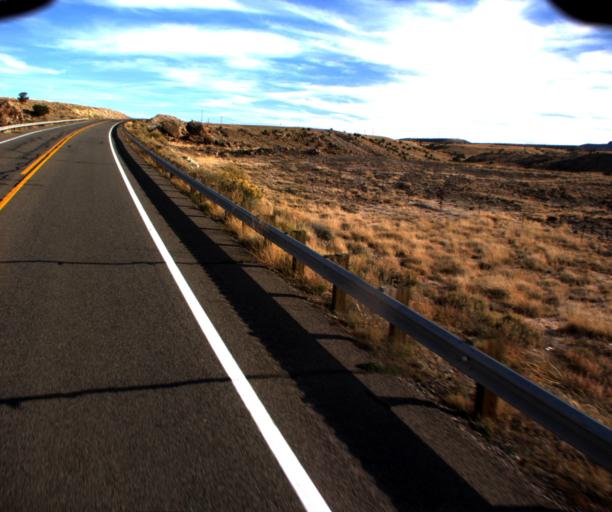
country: US
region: New Mexico
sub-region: San Juan County
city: Shiprock
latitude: 36.9153
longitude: -109.0776
